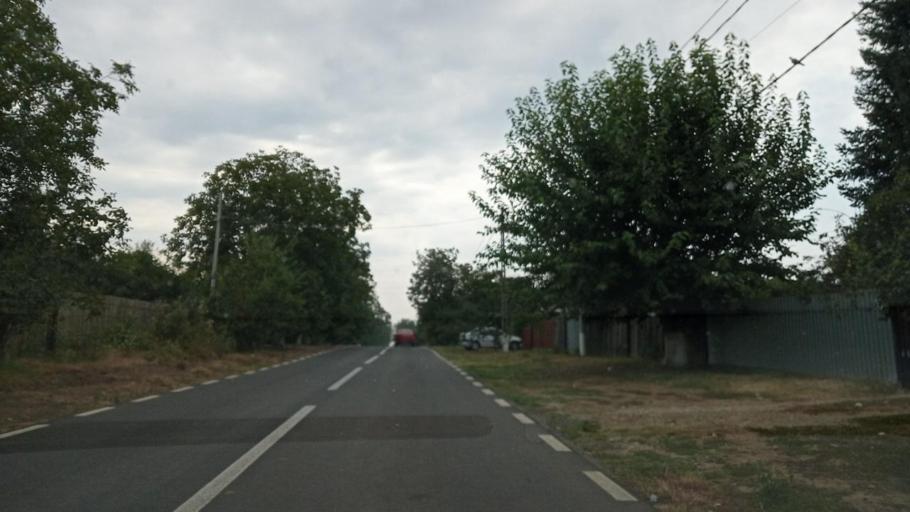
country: RO
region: Giurgiu
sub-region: Comuna Gostinari
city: Gostinari
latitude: 44.1727
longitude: 26.2405
